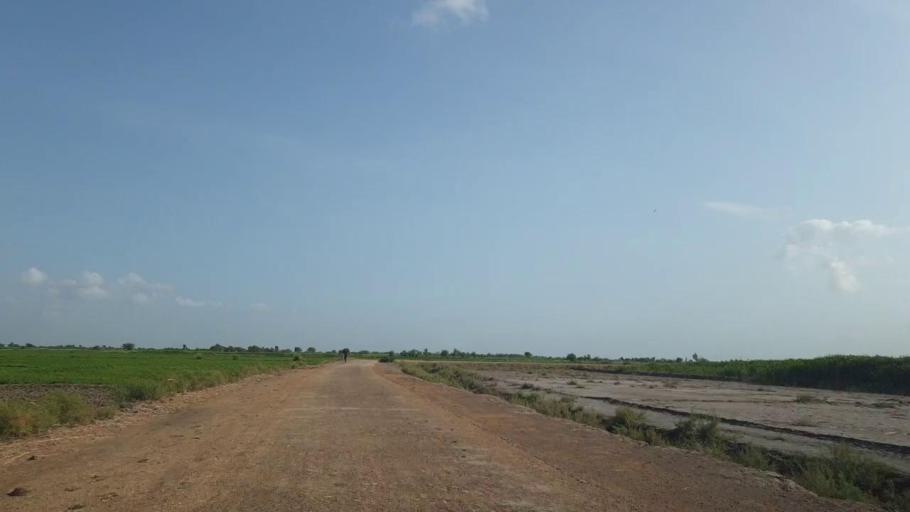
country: PK
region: Sindh
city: Kadhan
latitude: 24.6120
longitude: 69.0919
